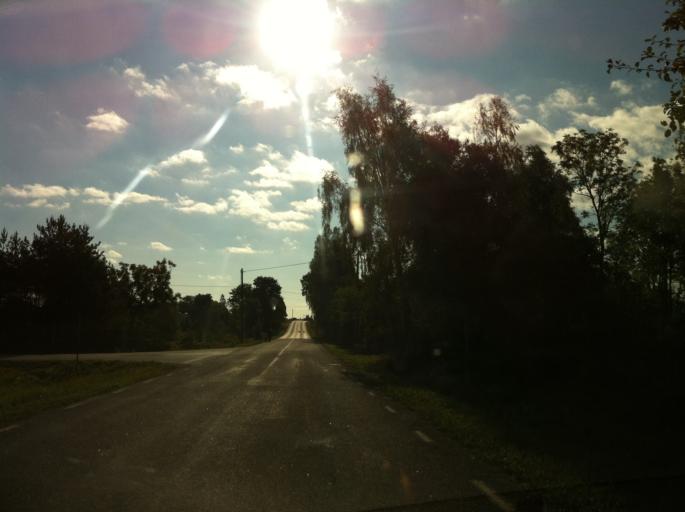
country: SE
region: Gotland
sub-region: Gotland
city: Slite
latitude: 57.4532
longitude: 18.7021
